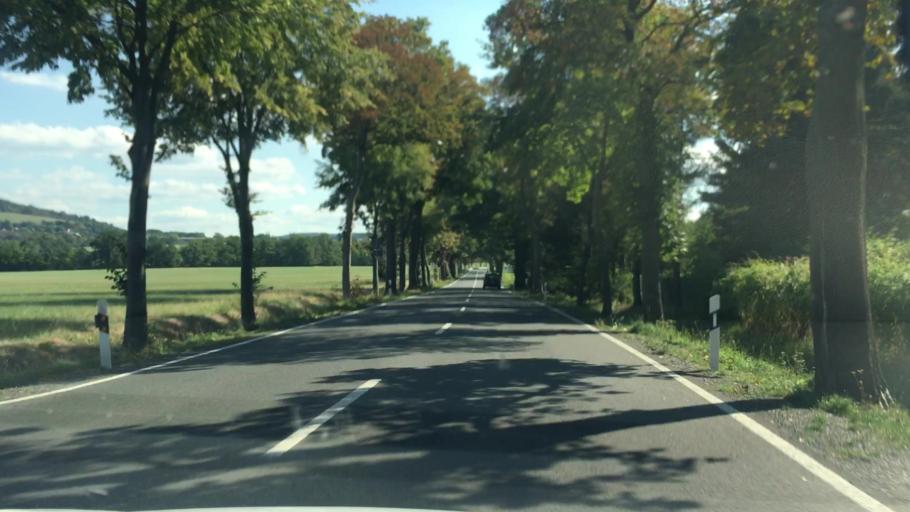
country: DE
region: Saxony
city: Dohma
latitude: 50.9122
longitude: 13.9453
